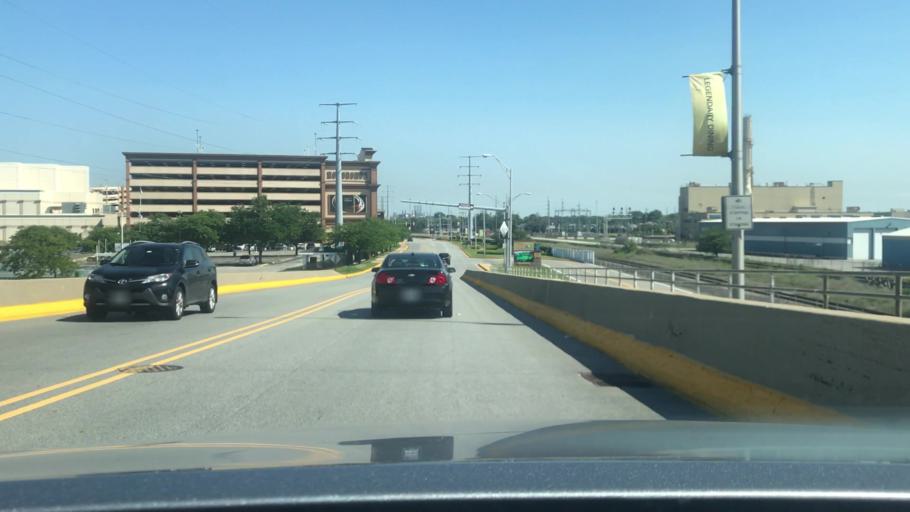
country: US
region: Indiana
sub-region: Lake County
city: Whiting
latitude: 41.6958
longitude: -87.5114
